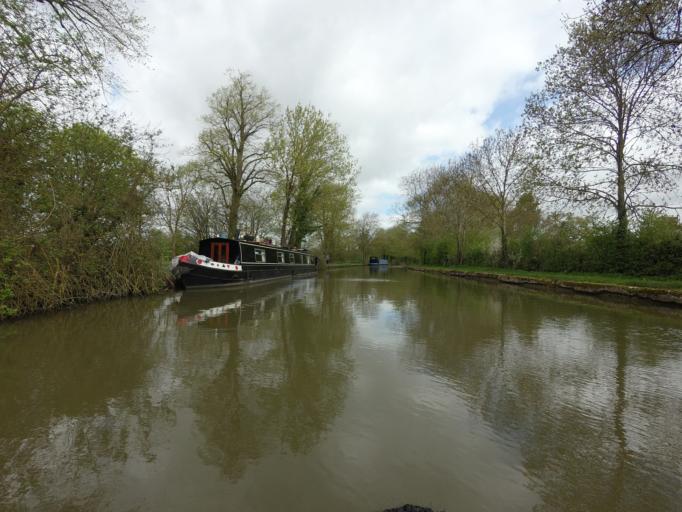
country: GB
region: England
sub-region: Milton Keynes
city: Water Eaton
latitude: 51.9689
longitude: -0.7168
